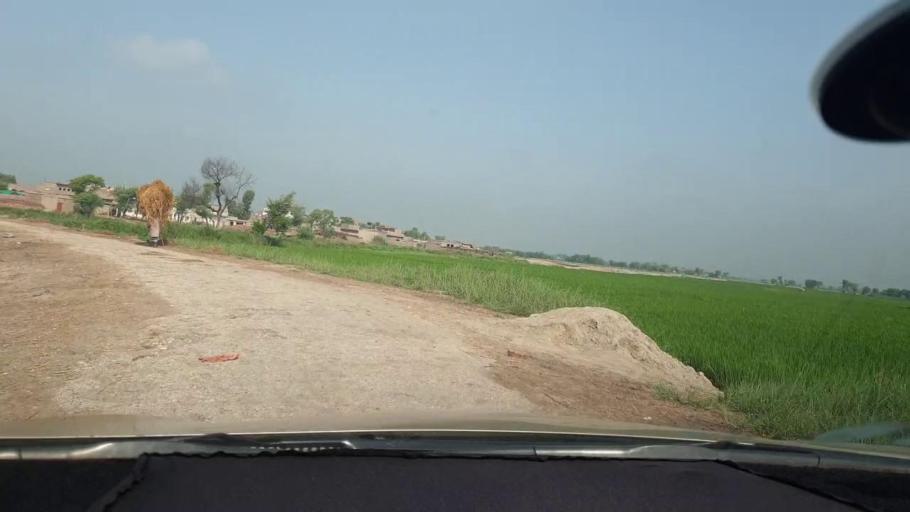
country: PK
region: Sindh
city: Kambar
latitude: 27.5416
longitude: 68.0496
